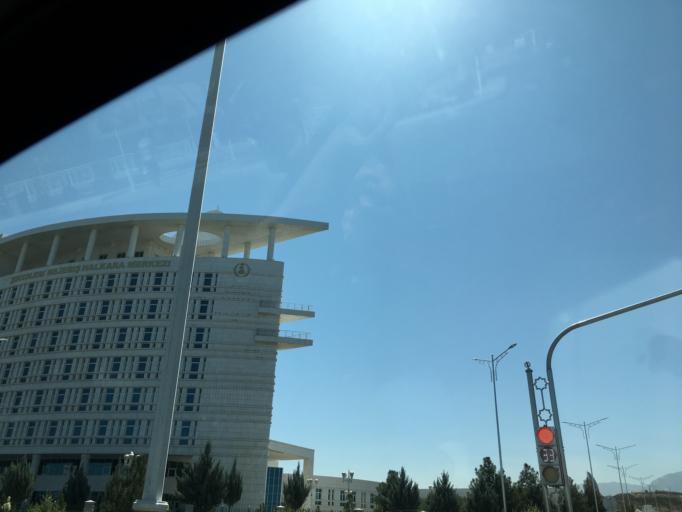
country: TM
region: Ahal
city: Ashgabat
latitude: 37.9520
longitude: 58.3392
